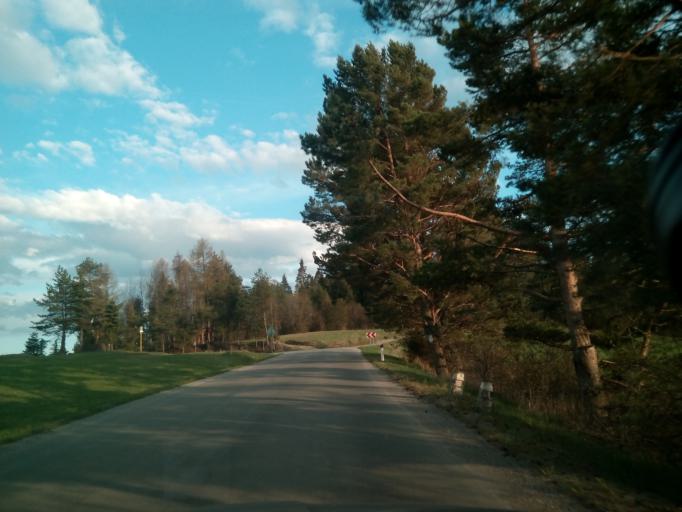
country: PL
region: Lesser Poland Voivodeship
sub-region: Powiat nowotarski
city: Niedzica
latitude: 49.3316
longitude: 20.3139
